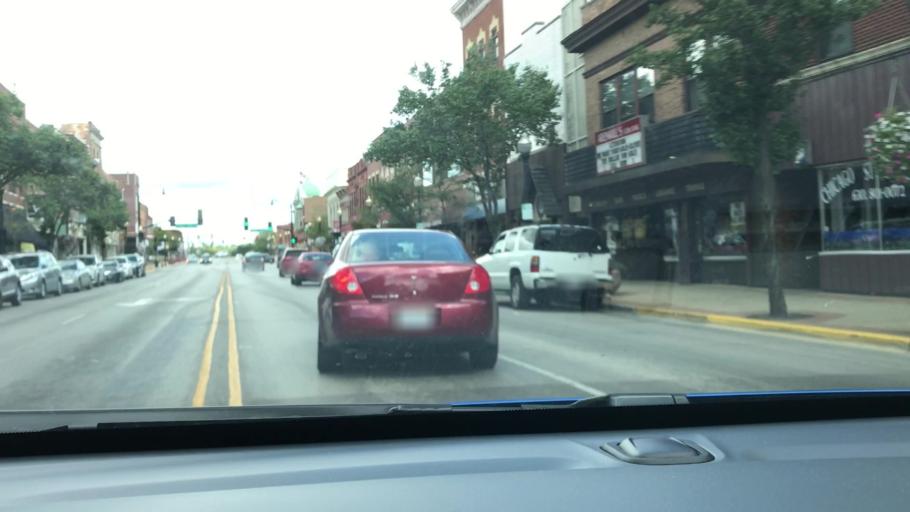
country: US
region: Illinois
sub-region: Kane County
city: Aurora
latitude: 41.7573
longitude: -88.3128
